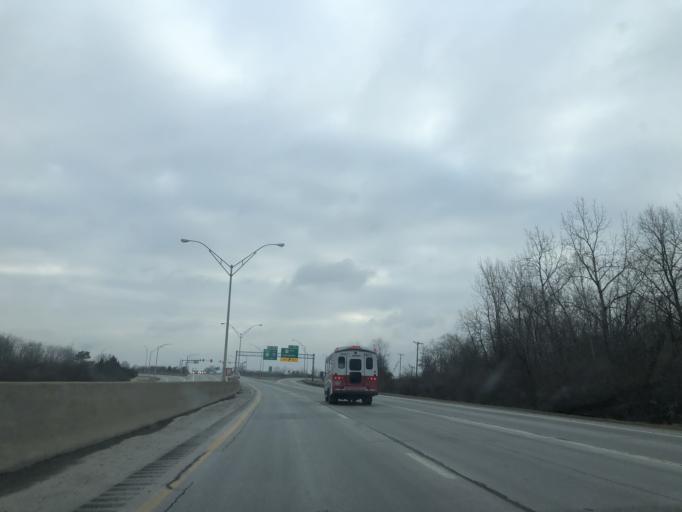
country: US
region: Ohio
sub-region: Franklin County
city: Obetz
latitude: 39.9180
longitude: -82.9250
